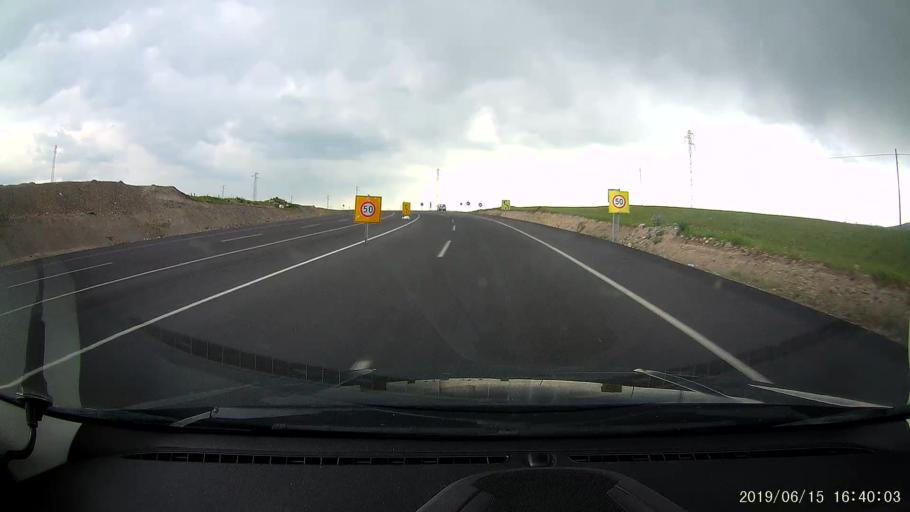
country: TR
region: Ardahan
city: Haskoy
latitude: 40.9744
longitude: 42.8933
